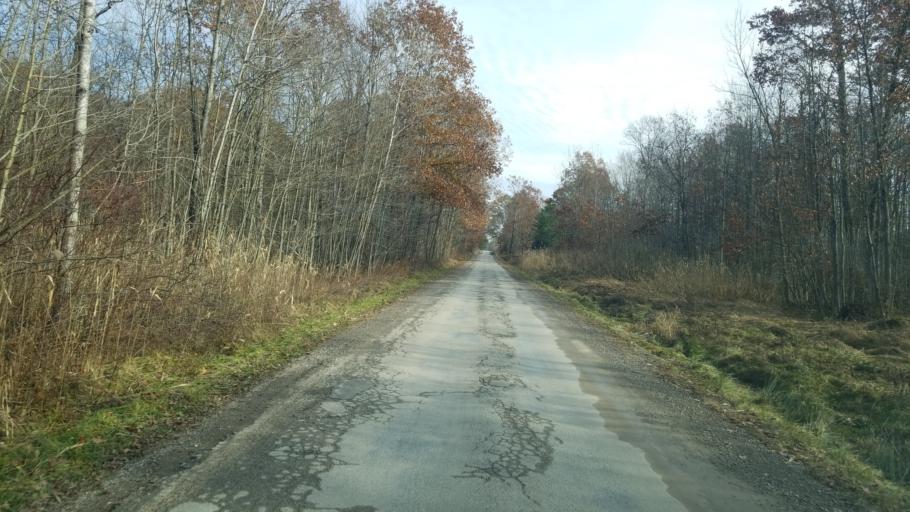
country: US
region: Ohio
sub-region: Ashtabula County
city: Roaming Shores
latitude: 41.6432
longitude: -80.7904
